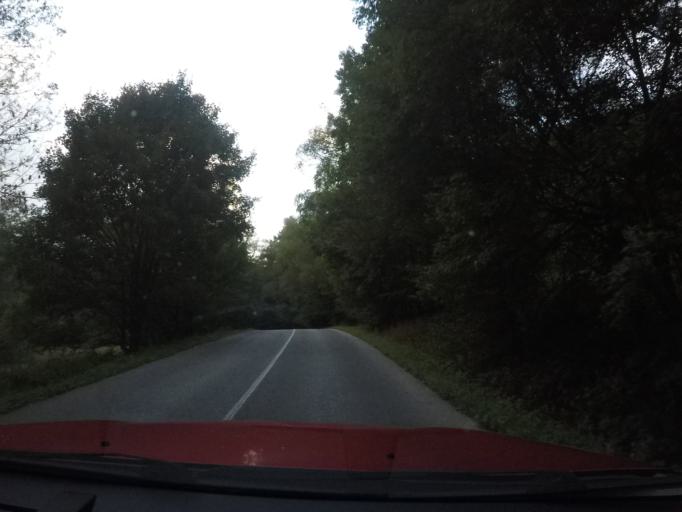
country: SK
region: Kosicky
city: Roznava
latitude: 48.6470
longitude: 20.6908
